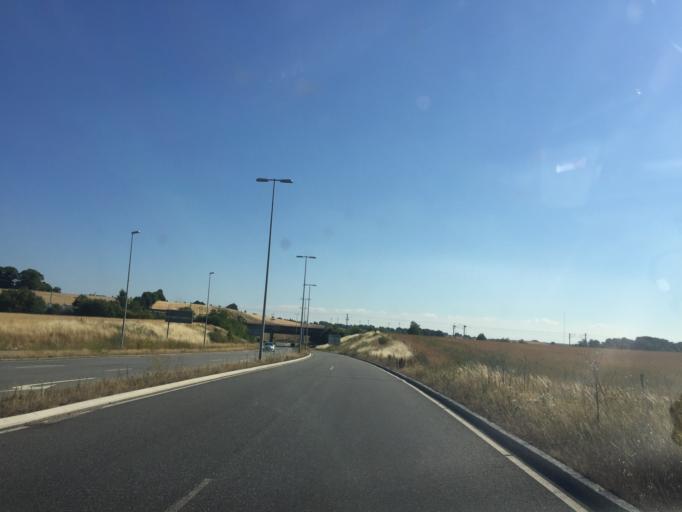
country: DK
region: Capital Region
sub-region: Egedal Kommune
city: Smorumnedre
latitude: 55.7541
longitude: 12.2869
